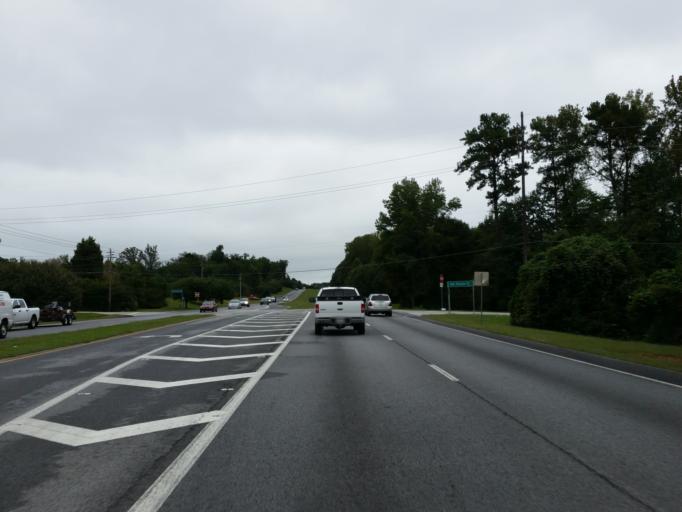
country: US
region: Georgia
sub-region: Clayton County
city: Jonesboro
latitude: 33.5024
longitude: -84.3501
